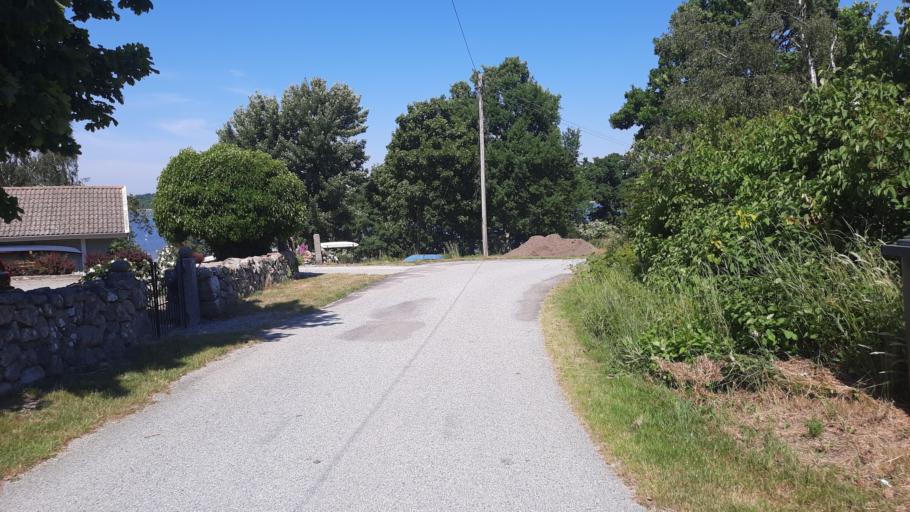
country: SE
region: Blekinge
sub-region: Karlskrona Kommun
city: Jaemjoe
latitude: 56.1530
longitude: 15.7585
